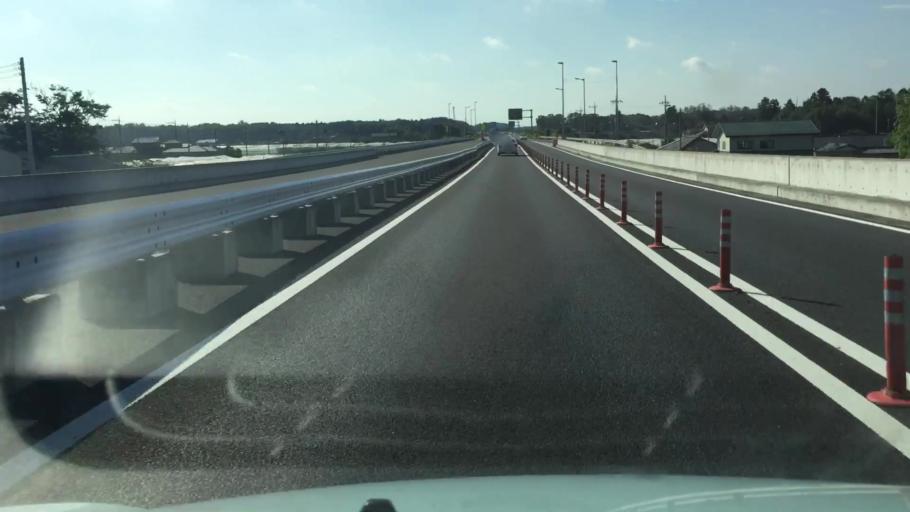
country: JP
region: Tochigi
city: Mooka
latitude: 36.5095
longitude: 139.9872
